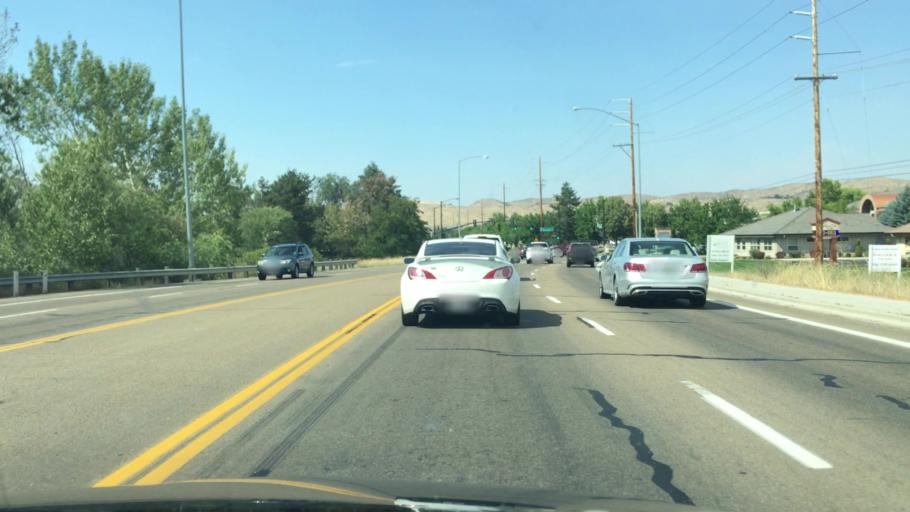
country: US
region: Idaho
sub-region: Ada County
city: Garden City
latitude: 43.6620
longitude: -116.2796
